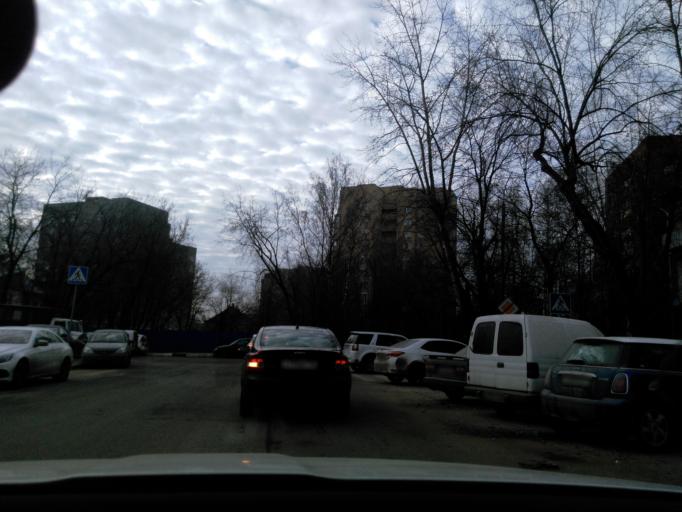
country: RU
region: Moskovskaya
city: Levoberezhnaya
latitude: 55.8960
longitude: 37.4815
